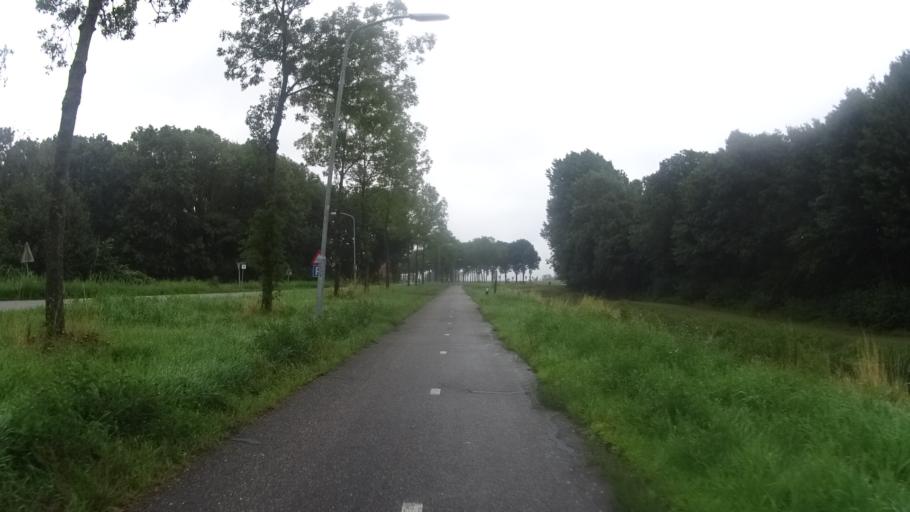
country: NL
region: Groningen
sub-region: Gemeente  Oldambt
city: Winschoten
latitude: 53.1543
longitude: 7.0713
